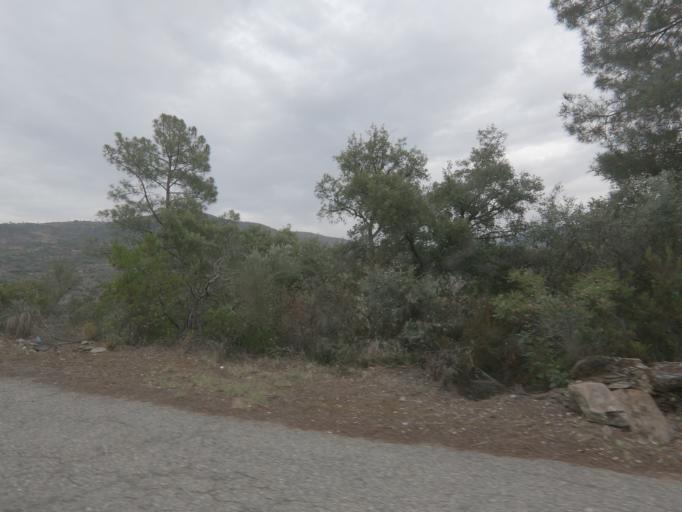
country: PT
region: Viseu
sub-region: Armamar
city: Armamar
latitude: 41.1434
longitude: -7.6448
